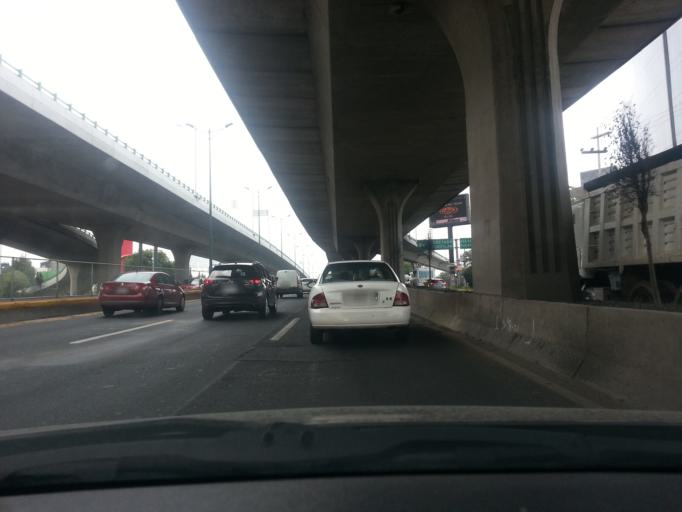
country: MX
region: Mexico
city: Naucalpan de Juarez
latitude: 19.4781
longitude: -99.2310
